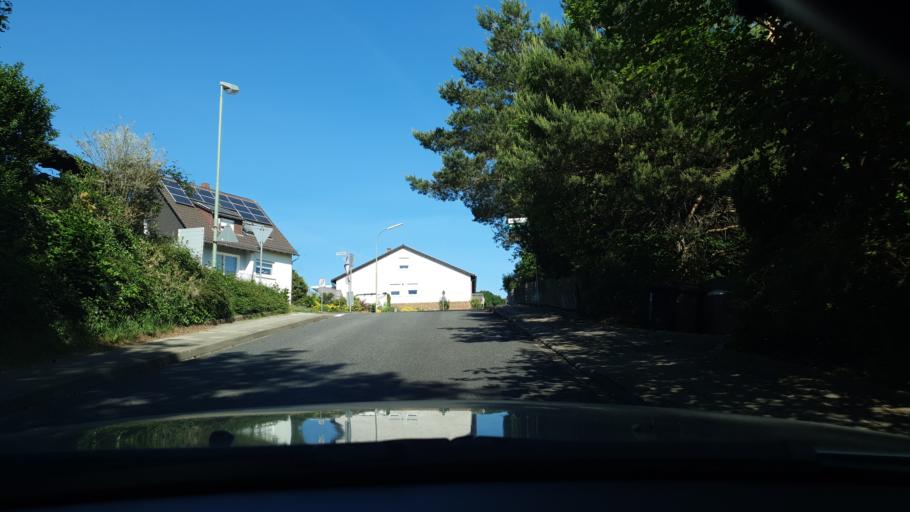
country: DE
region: Rheinland-Pfalz
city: Otterberg
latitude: 49.4792
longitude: 7.7815
